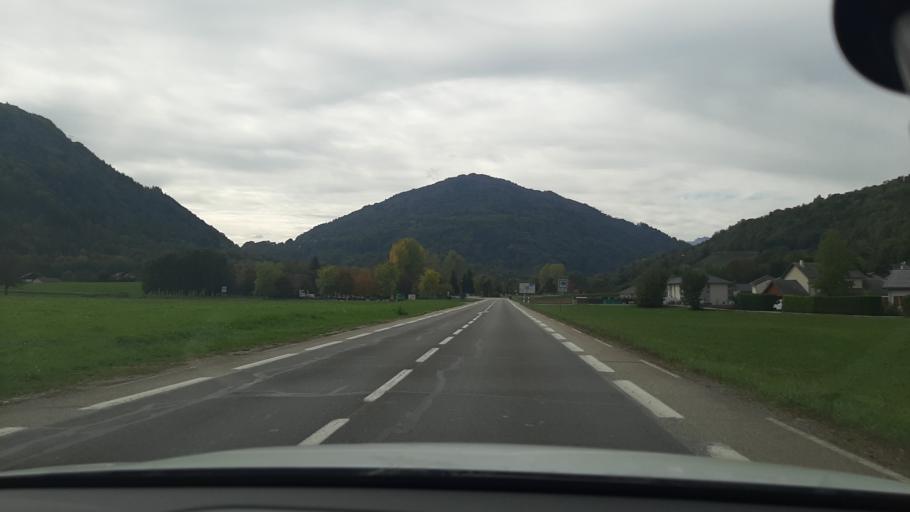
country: FR
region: Rhone-Alpes
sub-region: Departement de la Savoie
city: La Rochette
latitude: 45.4552
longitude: 6.1060
